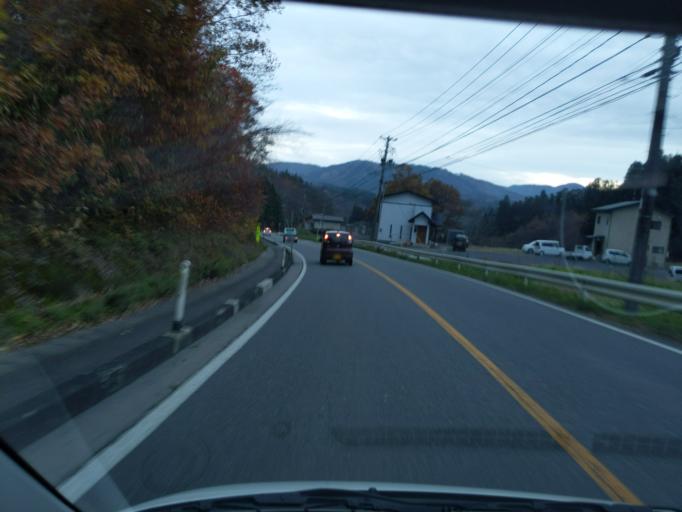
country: JP
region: Iwate
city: Ichinoseki
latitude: 39.0009
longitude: 141.3237
